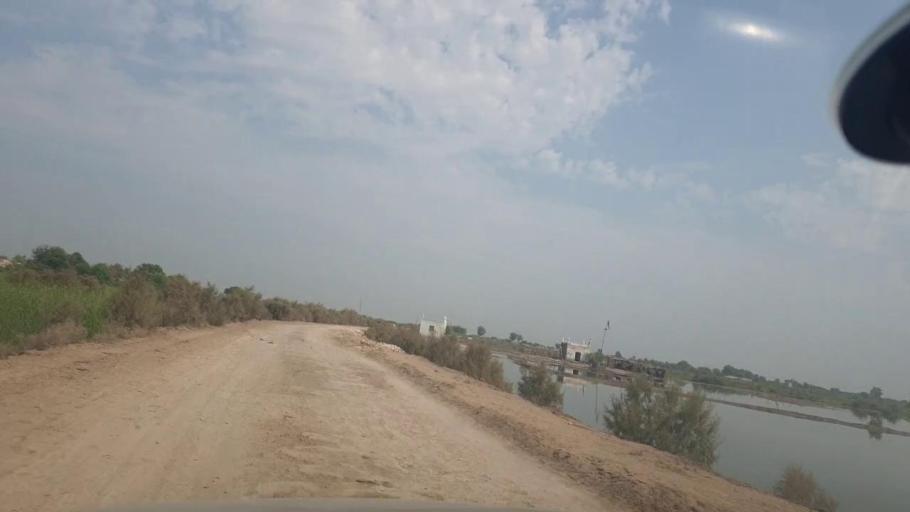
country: PK
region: Balochistan
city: Mehrabpur
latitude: 28.1109
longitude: 68.0903
